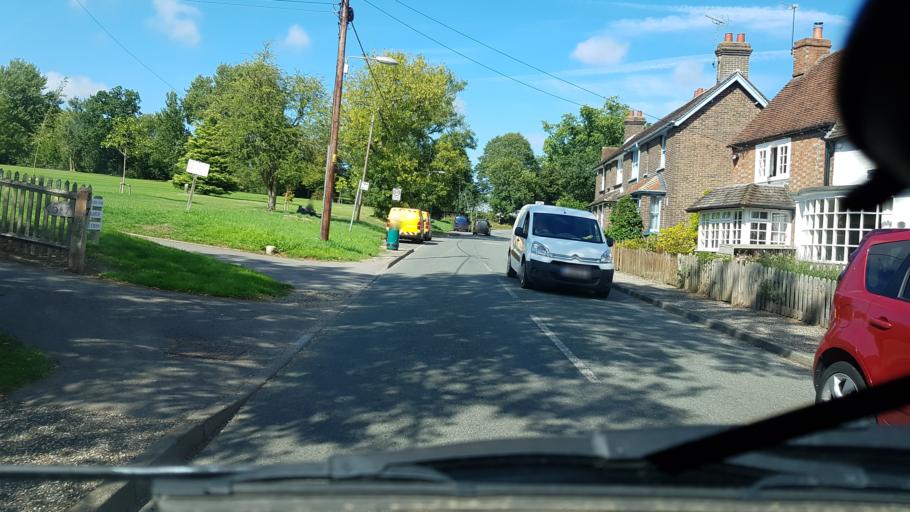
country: GB
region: England
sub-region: West Sussex
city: Horsham
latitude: 51.0919
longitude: -0.3464
